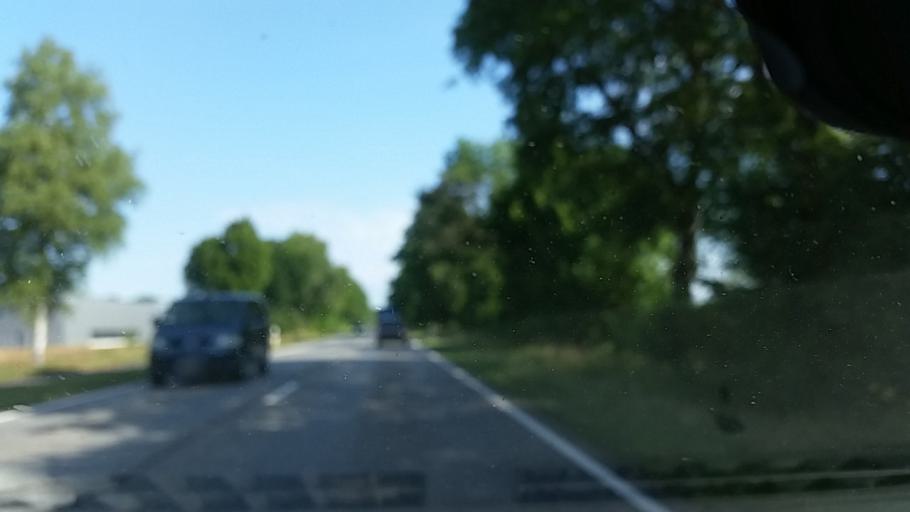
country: DE
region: Schleswig-Holstein
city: Tangstedt
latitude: 53.7190
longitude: 10.0281
